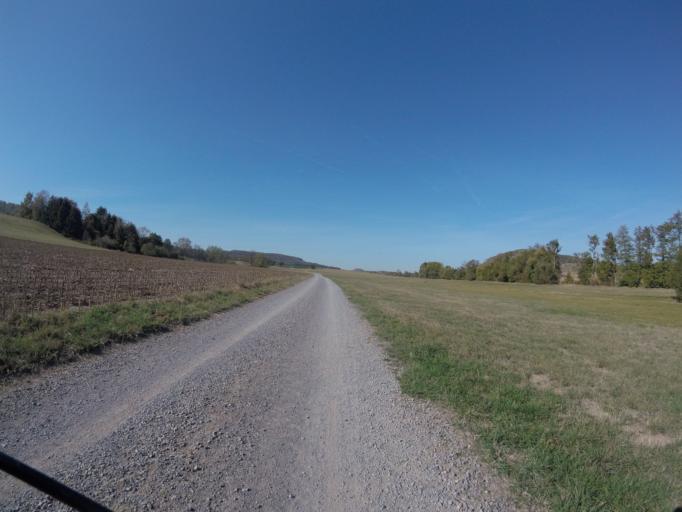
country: DE
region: Baden-Wuerttemberg
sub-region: Karlsruhe Region
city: Illingen
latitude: 48.9904
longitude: 8.9252
